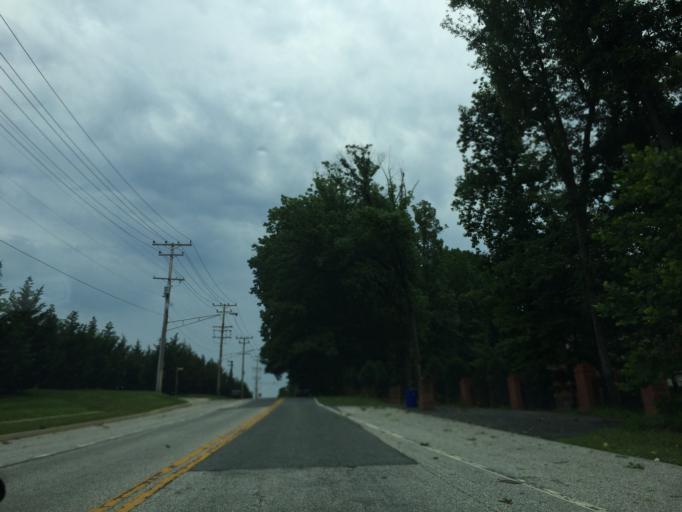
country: US
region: Maryland
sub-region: Howard County
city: Riverside
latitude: 39.1760
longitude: -76.8983
